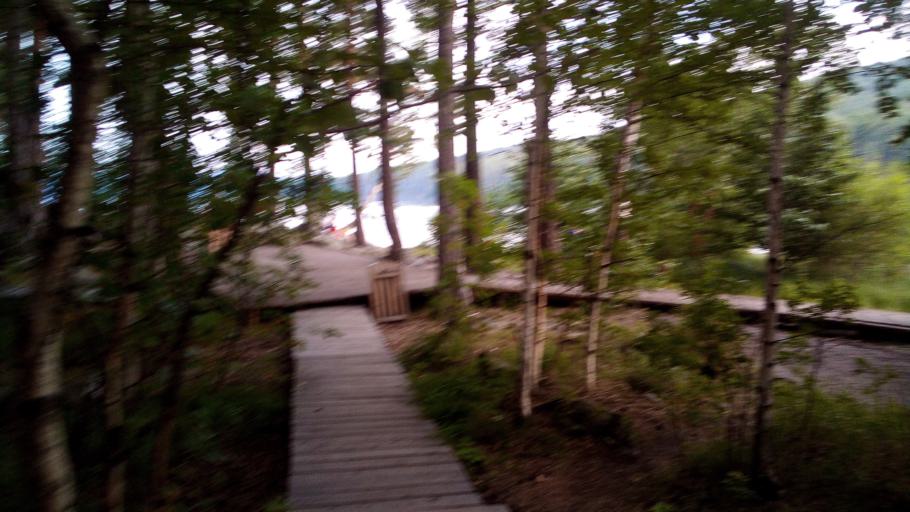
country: RU
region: Chelyabinsk
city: Turgoyak
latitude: 55.1601
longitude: 60.0315
